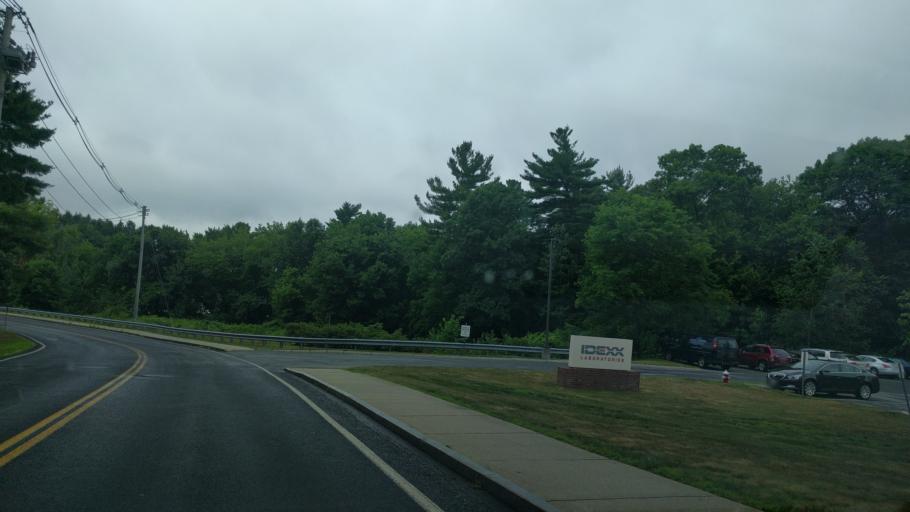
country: US
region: Massachusetts
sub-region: Worcester County
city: Grafton
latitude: 42.2490
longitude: -71.6848
